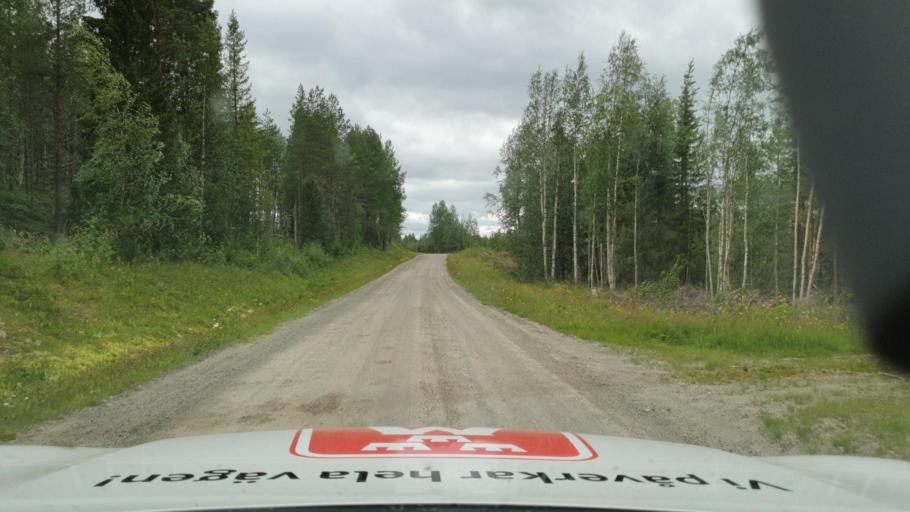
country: SE
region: Vaesterbotten
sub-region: Dorotea Kommun
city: Dorotea
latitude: 64.2076
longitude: 16.8058
